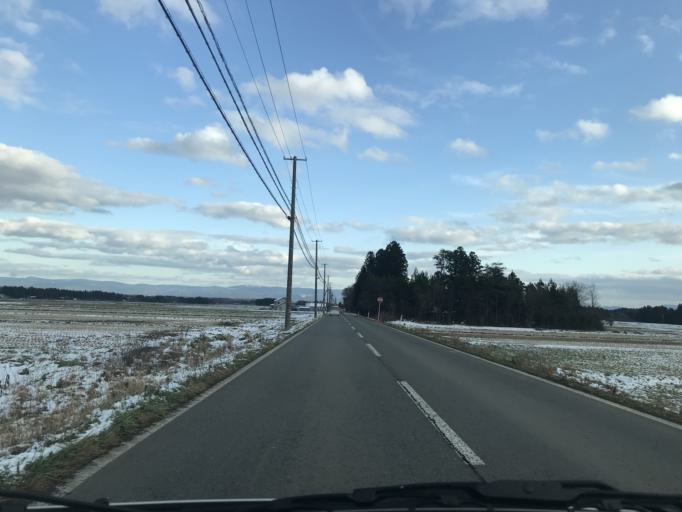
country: JP
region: Iwate
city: Kitakami
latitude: 39.2120
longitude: 141.0307
